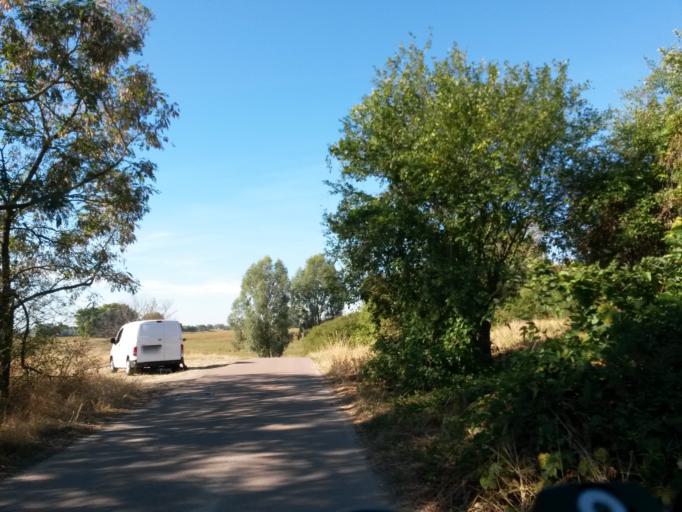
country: DE
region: Saxony-Anhalt
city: Wittenburg
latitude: 51.8708
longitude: 12.5600
